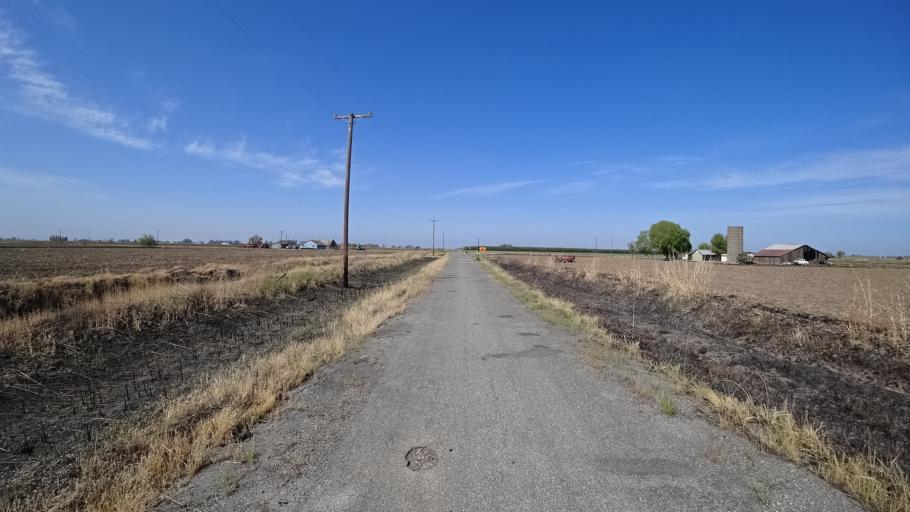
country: US
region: California
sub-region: Glenn County
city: Hamilton City
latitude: 39.6088
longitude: -122.0350
